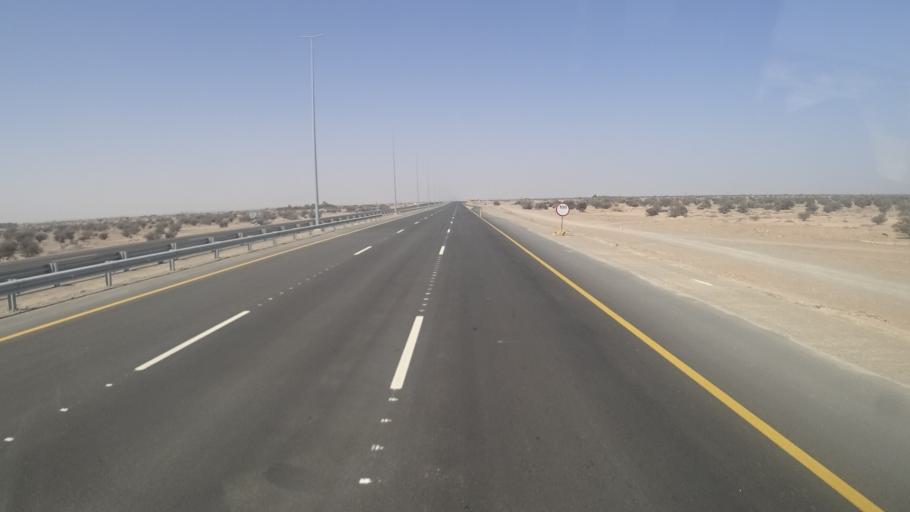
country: OM
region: Ash Sharqiyah
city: Sur
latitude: 22.2725
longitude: 59.2363
